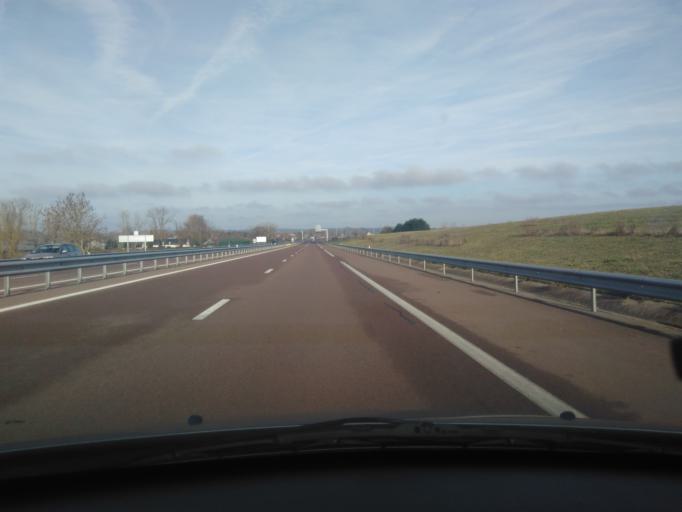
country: FR
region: Bourgogne
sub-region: Departement de la Nievre
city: Magny-Cours
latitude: 46.8657
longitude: 3.1500
